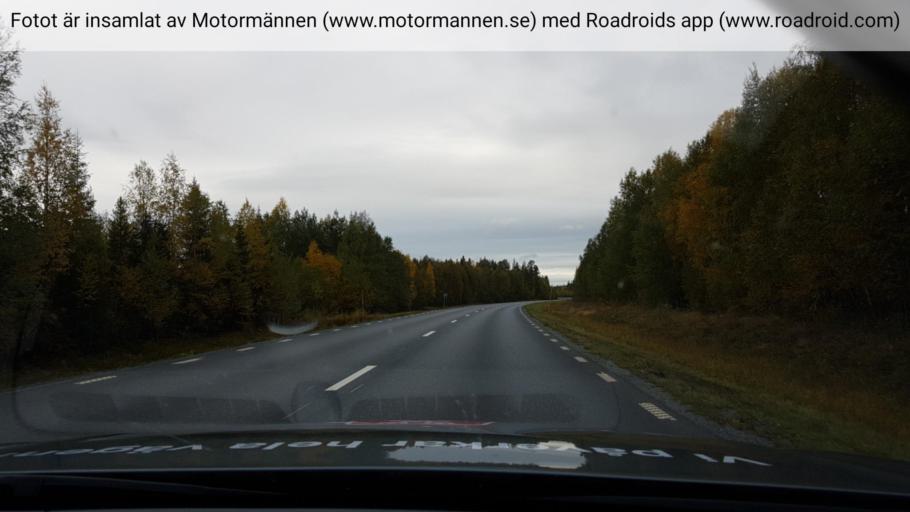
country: SE
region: Vaesterbotten
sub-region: Dorotea Kommun
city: Dorotea
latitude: 64.3459
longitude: 16.6524
